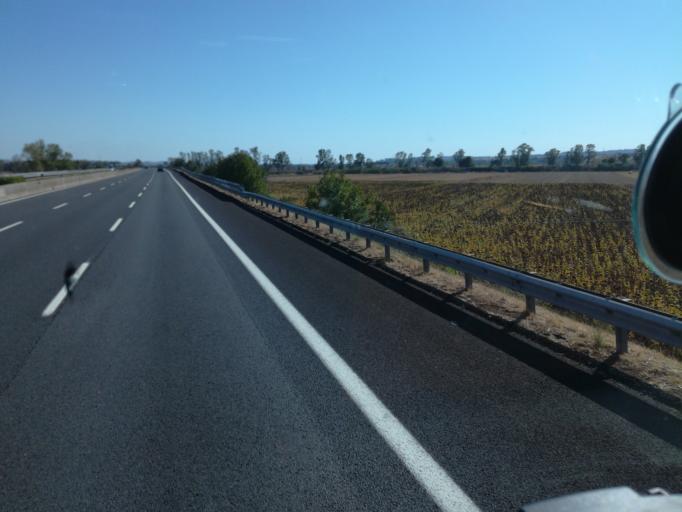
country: IT
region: Latium
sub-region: Citta metropolitana di Roma Capitale
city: Fiano Romano
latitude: 42.1375
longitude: 12.6194
